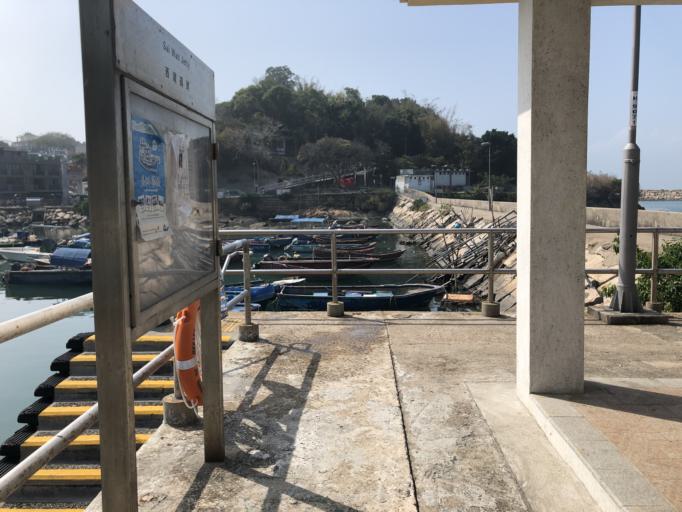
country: HK
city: Yung Shue Wan
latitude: 22.2012
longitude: 114.0208
